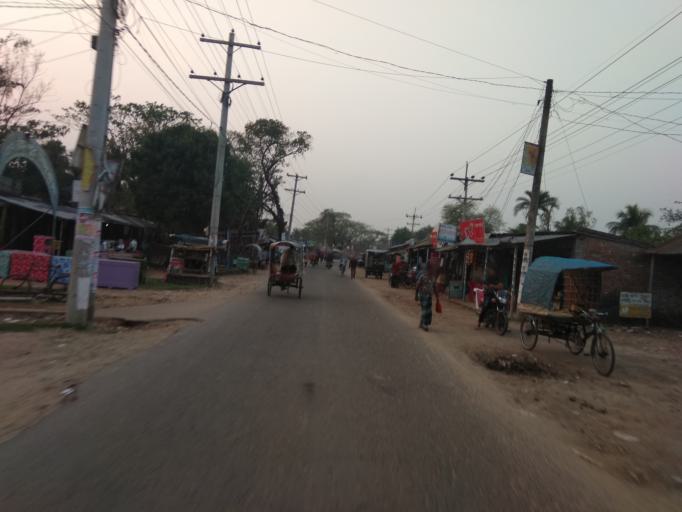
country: IN
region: West Bengal
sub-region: North 24 Parganas
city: Taki
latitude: 22.4529
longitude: 89.0352
